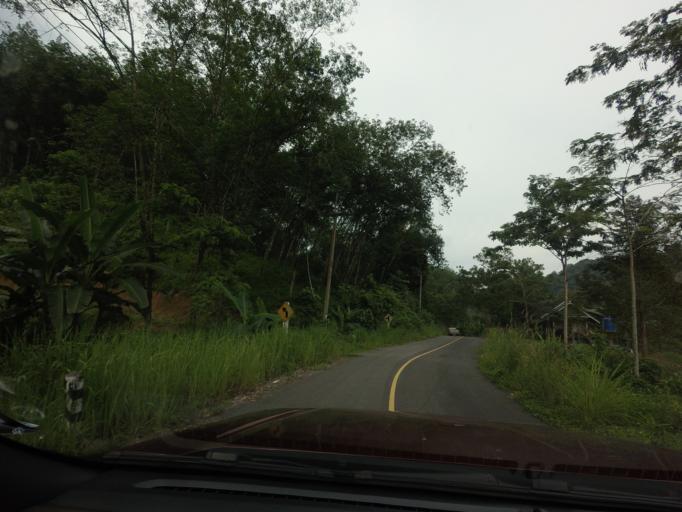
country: TH
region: Narathiwat
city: Si Sakhon
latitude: 6.0633
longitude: 101.3852
